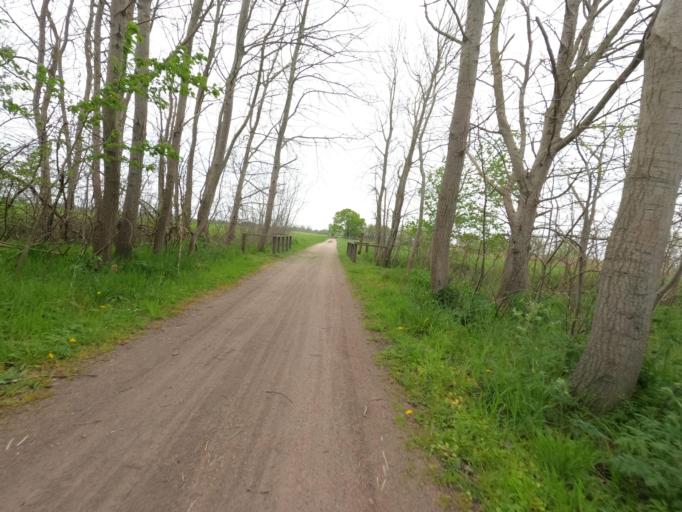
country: DE
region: Mecklenburg-Vorpommern
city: Ostseebad Dierhagen
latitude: 54.2800
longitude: 12.3773
